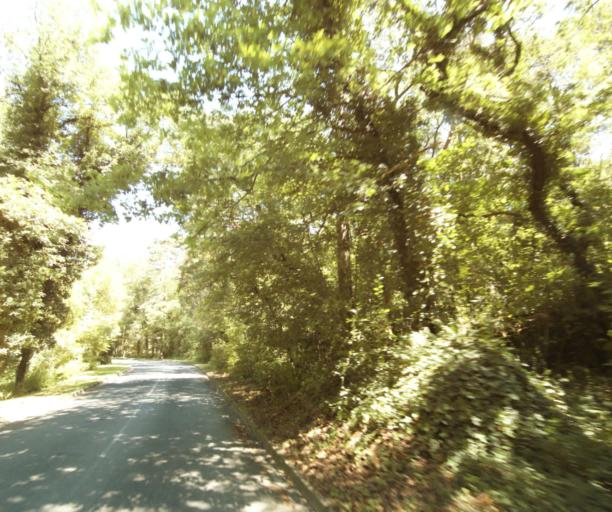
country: FR
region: Centre
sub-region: Departement du Loiret
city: Malesherbes
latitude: 48.2967
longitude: 2.4419
